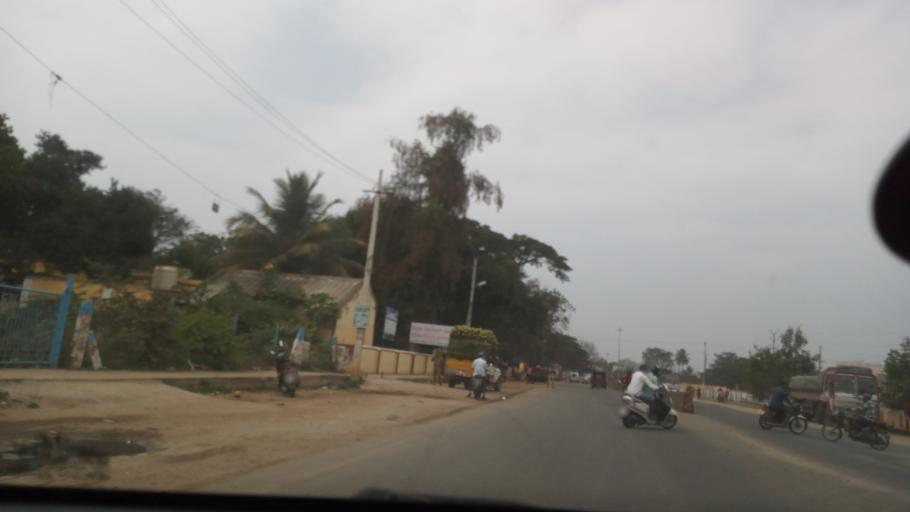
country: IN
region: Karnataka
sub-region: Chamrajnagar
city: Chamrajnagar
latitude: 11.9194
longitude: 76.9398
